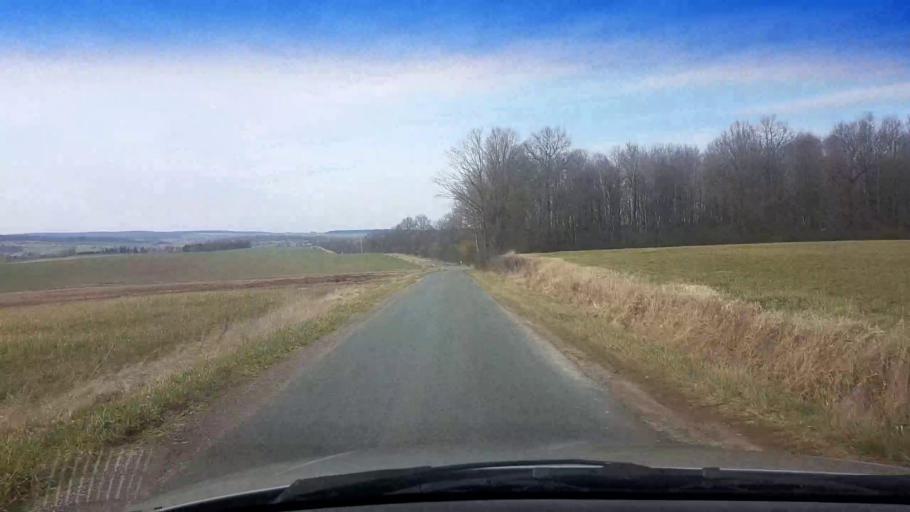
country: DE
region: Bavaria
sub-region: Upper Franconia
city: Burgebrach
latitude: 49.8104
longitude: 10.7599
